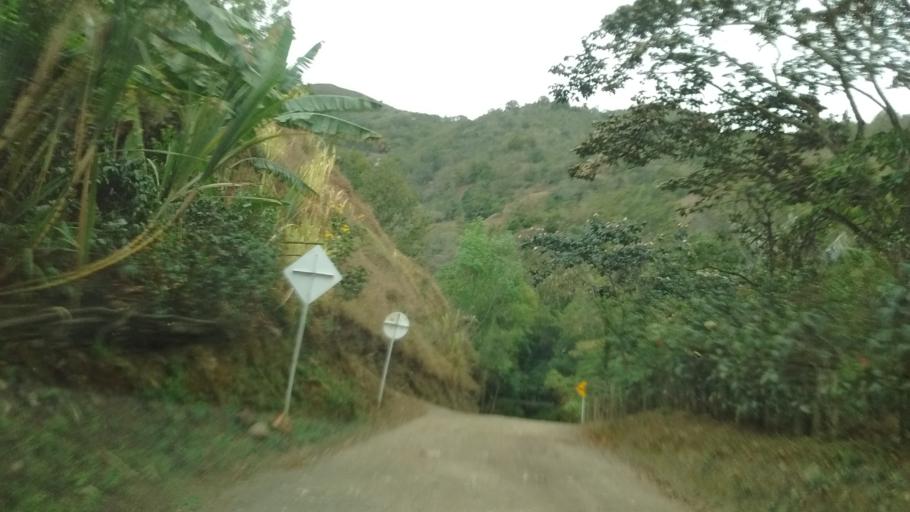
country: CO
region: Cauca
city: Almaguer
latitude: 1.8457
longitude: -76.9229
